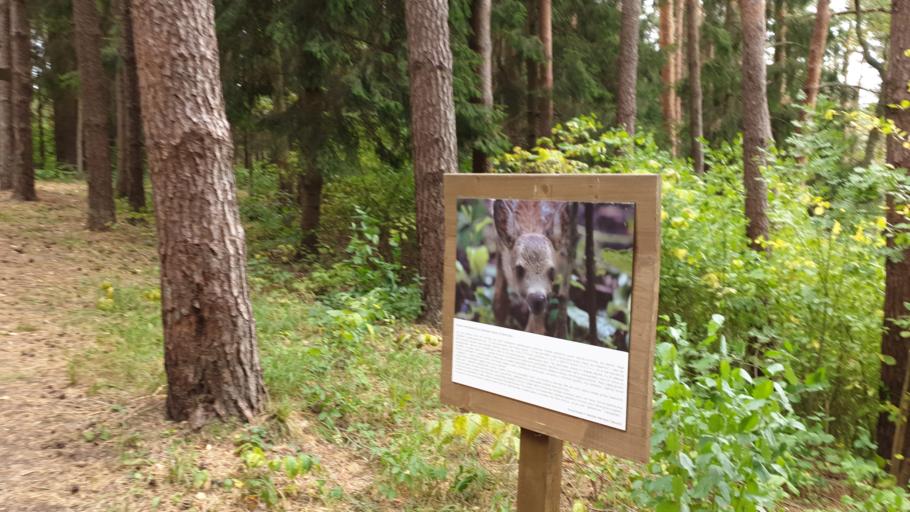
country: LT
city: Grigiskes
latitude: 54.7401
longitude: 25.0241
